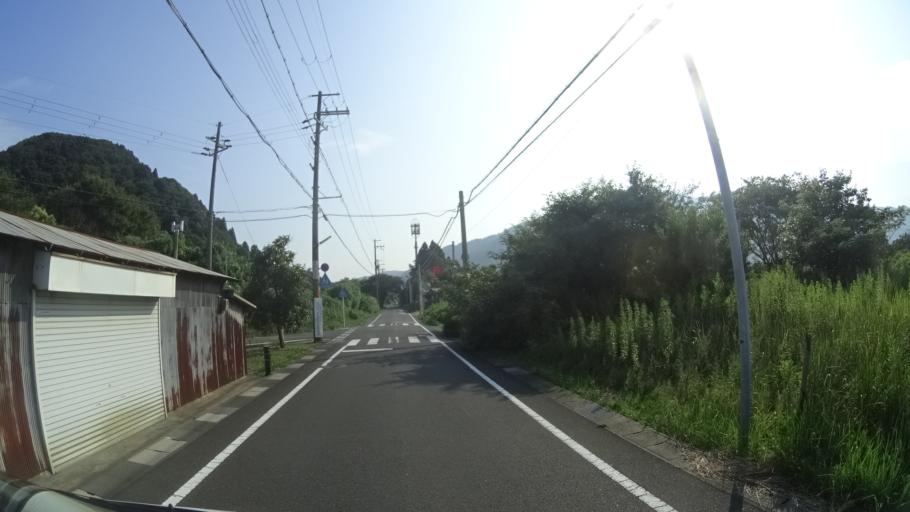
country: JP
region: Kyoto
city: Maizuru
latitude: 35.5104
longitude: 135.2951
